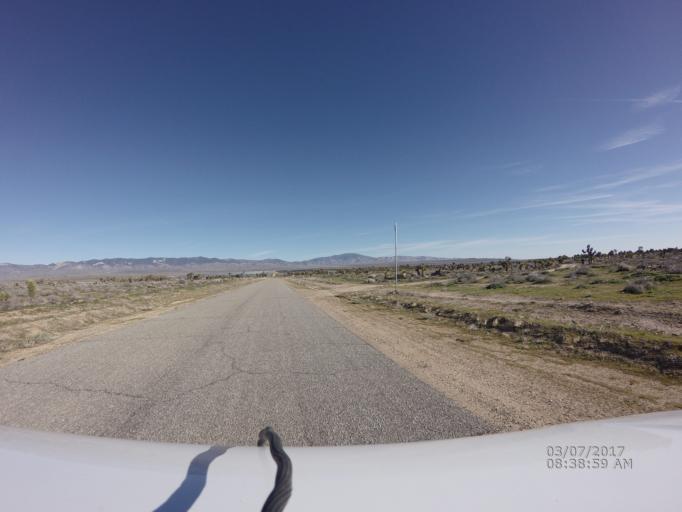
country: US
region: California
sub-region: Los Angeles County
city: Green Valley
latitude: 34.8023
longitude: -118.5457
